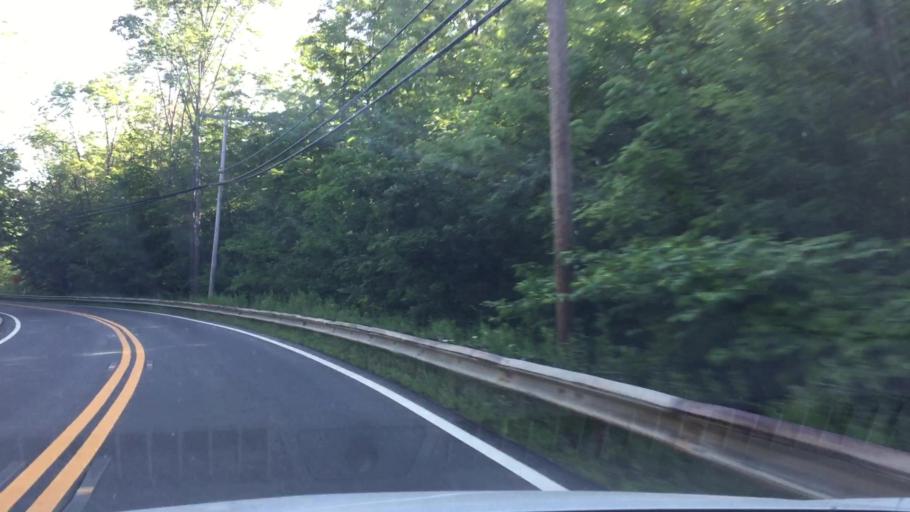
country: US
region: Massachusetts
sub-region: Berkshire County
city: Becket
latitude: 42.3232
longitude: -73.0846
